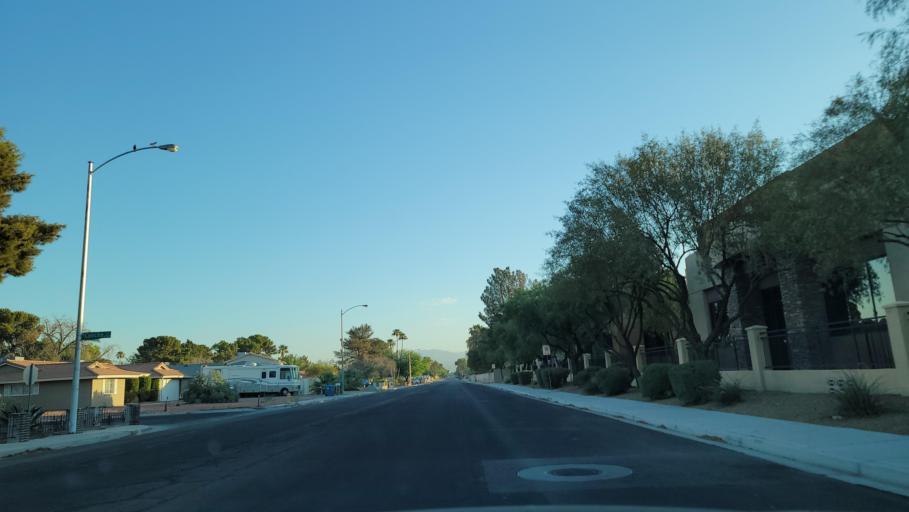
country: US
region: Nevada
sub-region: Clark County
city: Spring Valley
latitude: 36.1263
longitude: -115.2294
